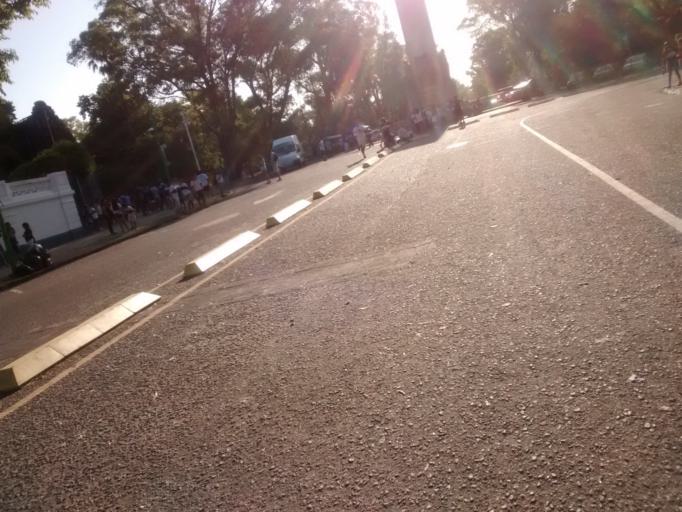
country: AR
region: Buenos Aires
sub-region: Partido de La Plata
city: La Plata
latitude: -34.9097
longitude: -57.9328
